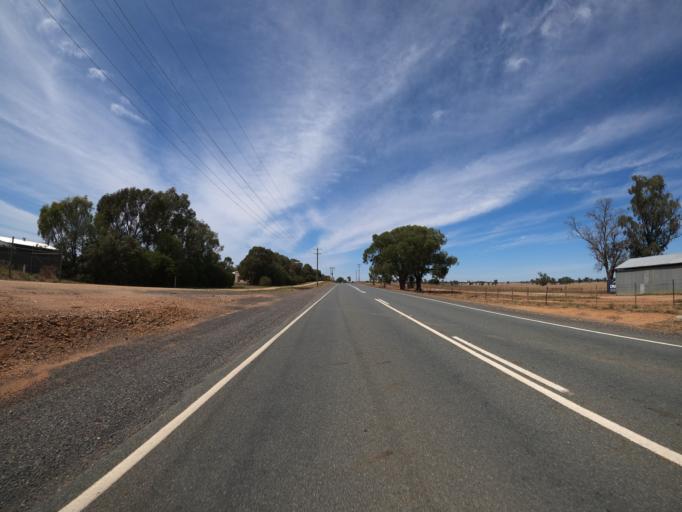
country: AU
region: Victoria
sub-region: Moira
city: Yarrawonga
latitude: -36.0457
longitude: 145.9955
